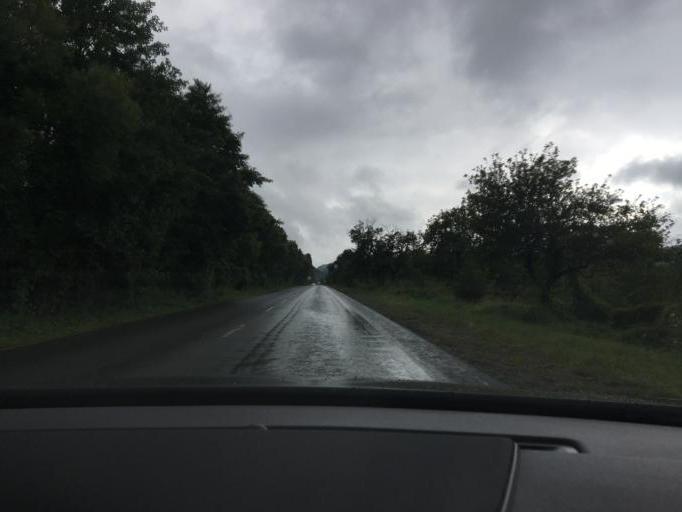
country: BG
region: Kyustendil
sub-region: Obshtina Kyustendil
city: Kyustendil
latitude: 42.2650
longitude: 22.5991
